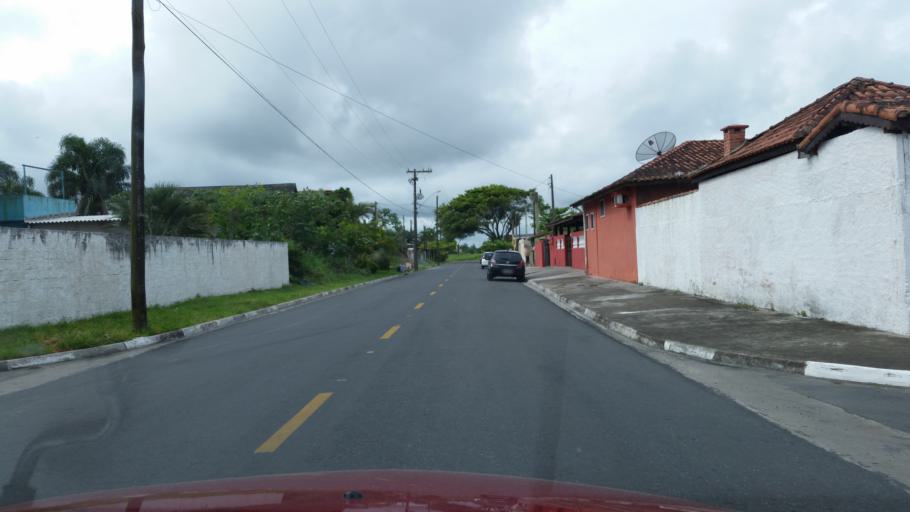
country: BR
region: Sao Paulo
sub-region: Iguape
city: Iguape
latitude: -24.7414
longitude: -47.5556
